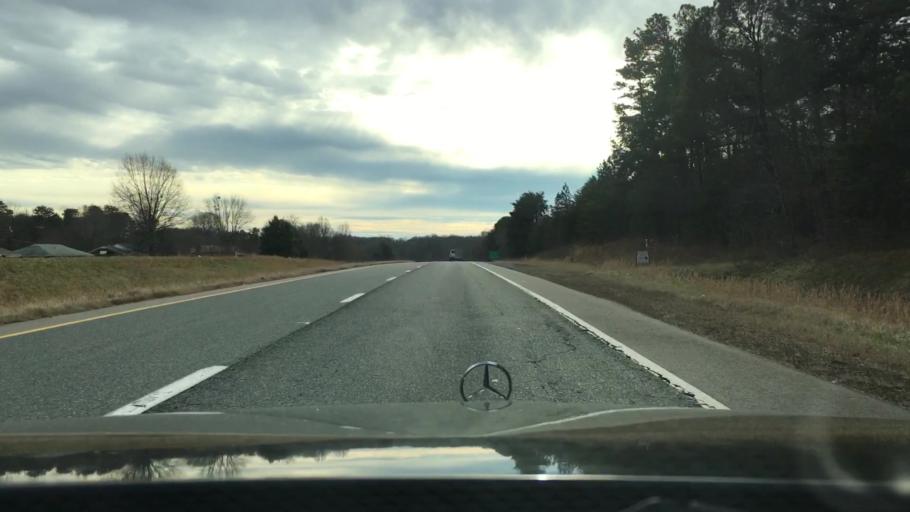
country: US
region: Virginia
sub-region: Pittsylvania County
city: Gretna
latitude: 36.9189
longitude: -79.3841
